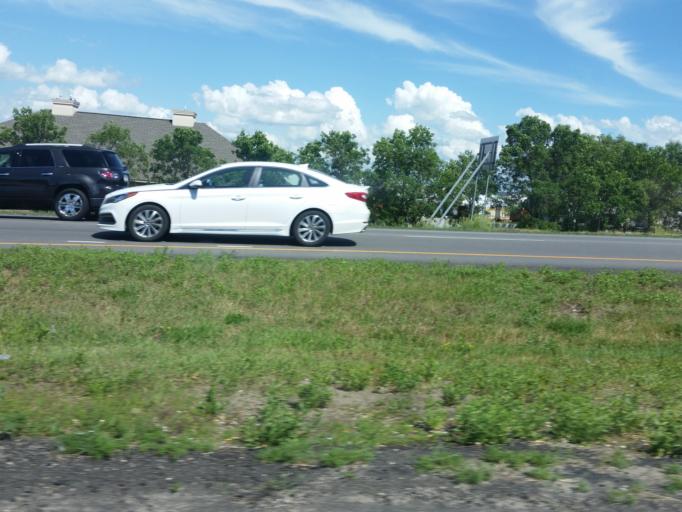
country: US
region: Minnesota
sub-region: Stearns County
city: Waite Park
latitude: 45.5644
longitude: -94.2060
